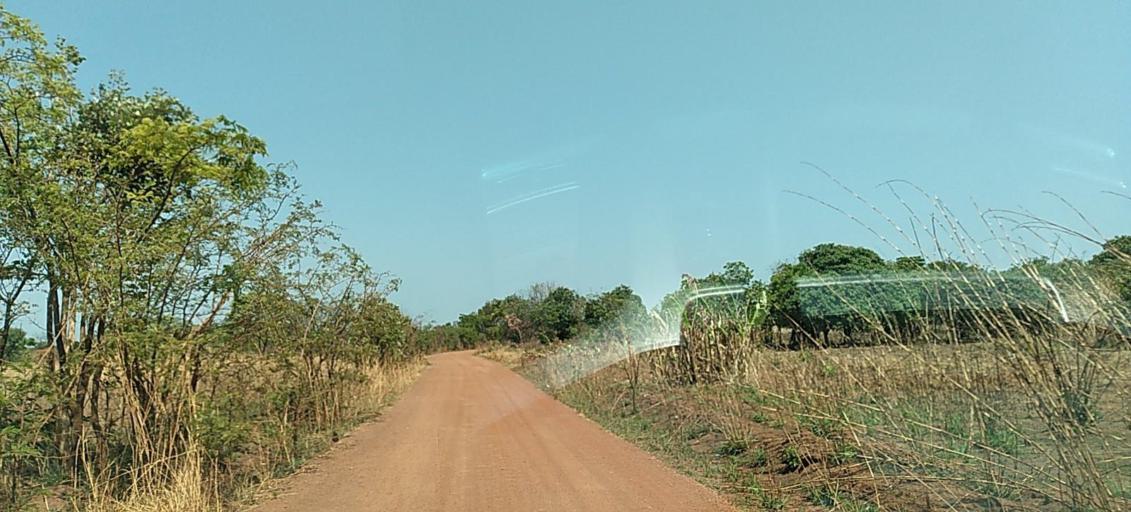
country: ZM
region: Copperbelt
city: Chingola
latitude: -12.5398
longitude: 27.7308
